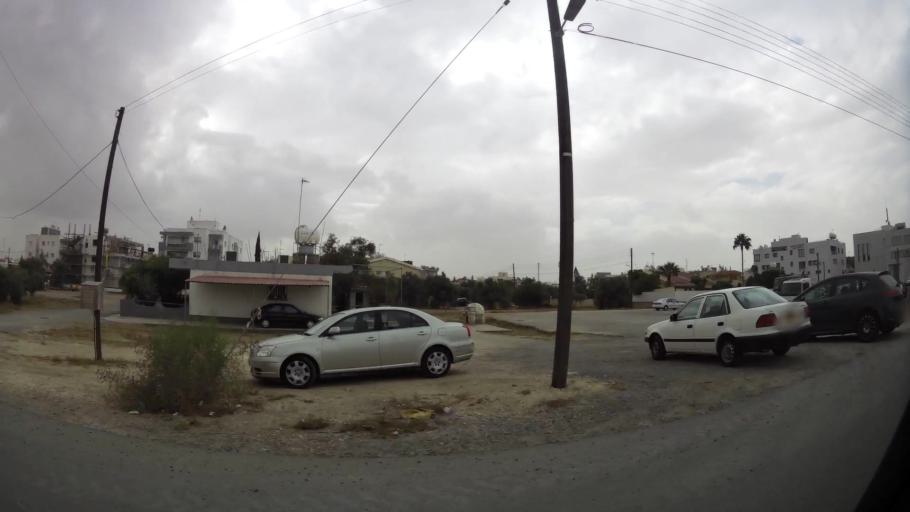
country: CY
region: Lefkosia
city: Geri
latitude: 35.1037
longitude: 33.3809
